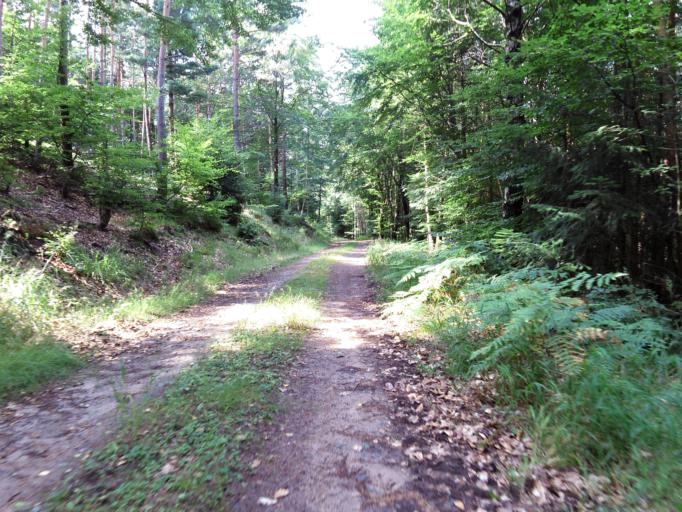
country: DE
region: Rheinland-Pfalz
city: Lindenberg
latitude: 49.4306
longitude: 8.0819
